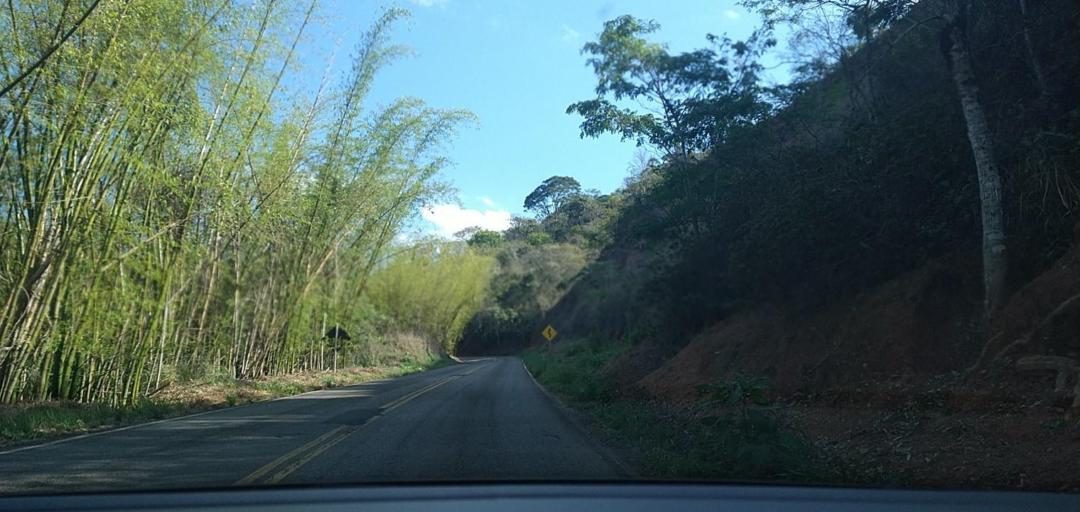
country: BR
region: Minas Gerais
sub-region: Alvinopolis
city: Alvinopolis
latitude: -20.1691
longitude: -42.9213
